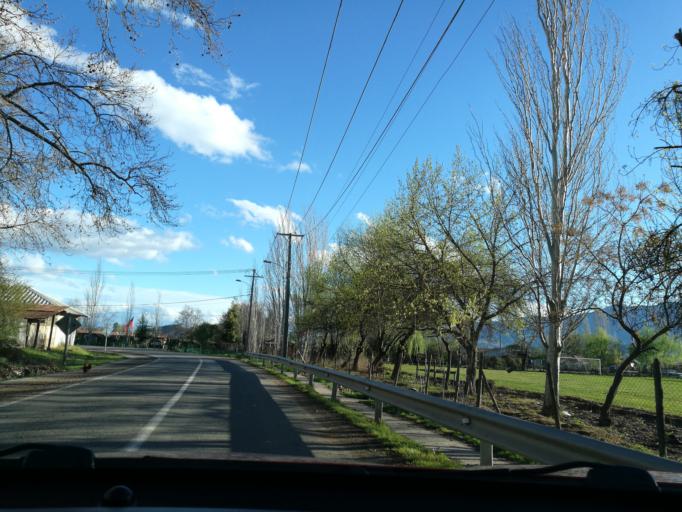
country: CL
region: O'Higgins
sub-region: Provincia de Cachapoal
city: Graneros
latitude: -34.1018
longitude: -70.8098
